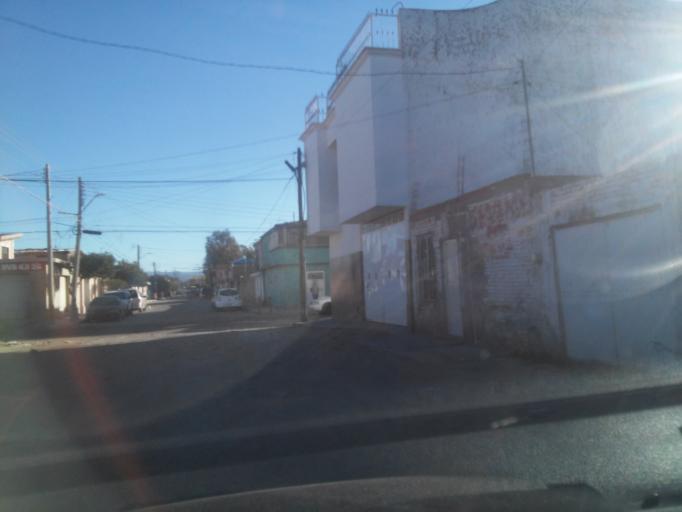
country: MX
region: Durango
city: Victoria de Durango
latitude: 24.0135
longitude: -104.6345
